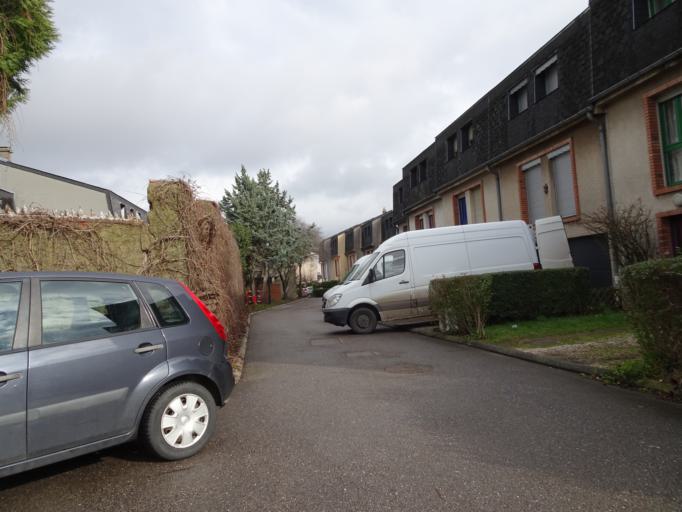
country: FR
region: Lorraine
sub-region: Departement de Meurthe-et-Moselle
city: Jarville-la-Malgrange
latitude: 48.6735
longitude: 6.1989
